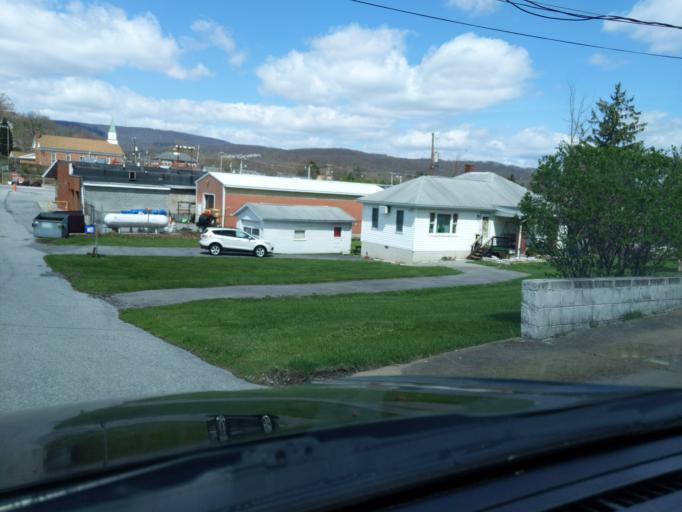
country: US
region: Pennsylvania
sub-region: Blair County
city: Altoona
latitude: 40.5334
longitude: -78.4016
